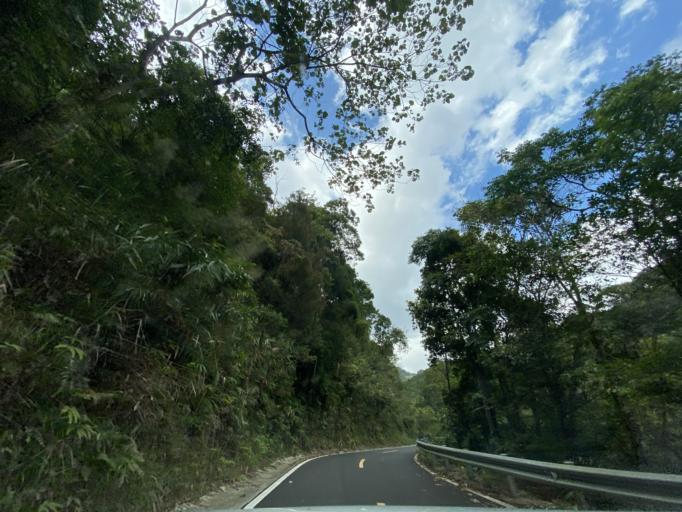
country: CN
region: Hainan
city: Benhao
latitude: 18.6948
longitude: 109.8804
